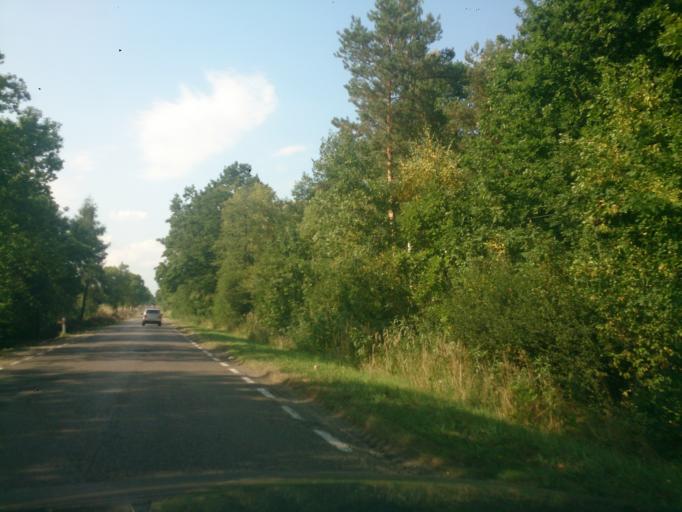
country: PL
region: Swietokrzyskie
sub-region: Powiat opatowski
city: Iwaniska
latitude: 50.7006
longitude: 21.3317
